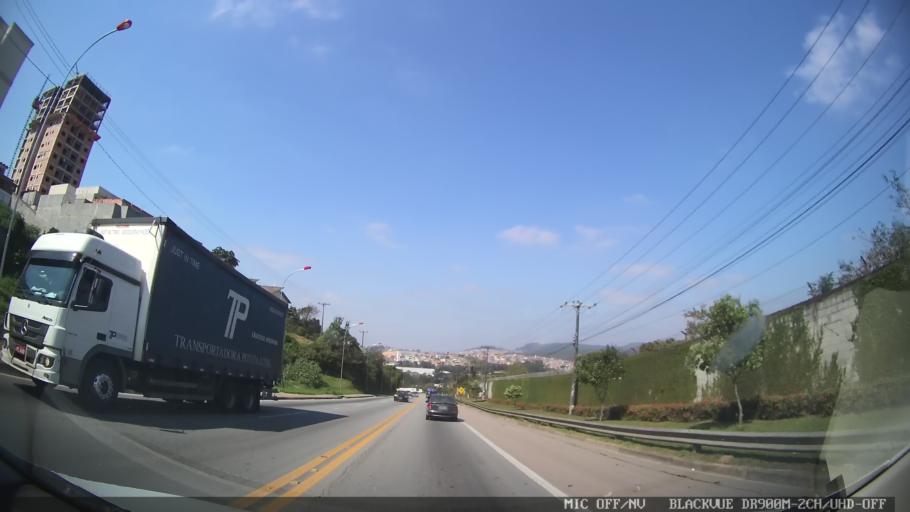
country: BR
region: Sao Paulo
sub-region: Franco Da Rocha
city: Franco da Rocha
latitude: -23.3217
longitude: -46.7538
